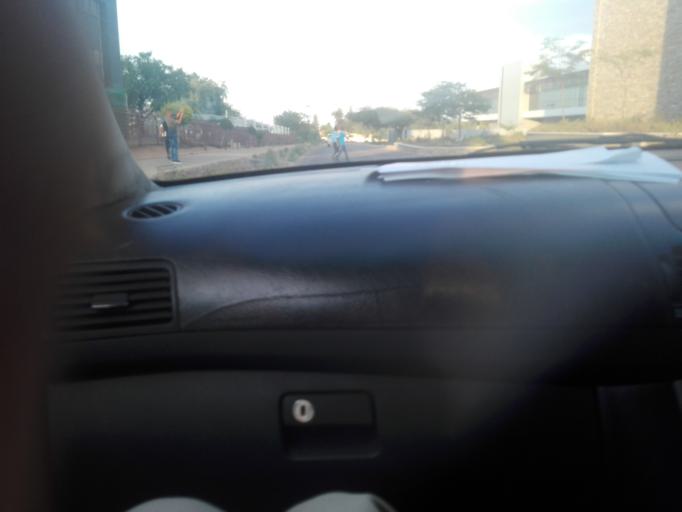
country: BW
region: South East
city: Gaborone
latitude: -24.6852
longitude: 25.8786
